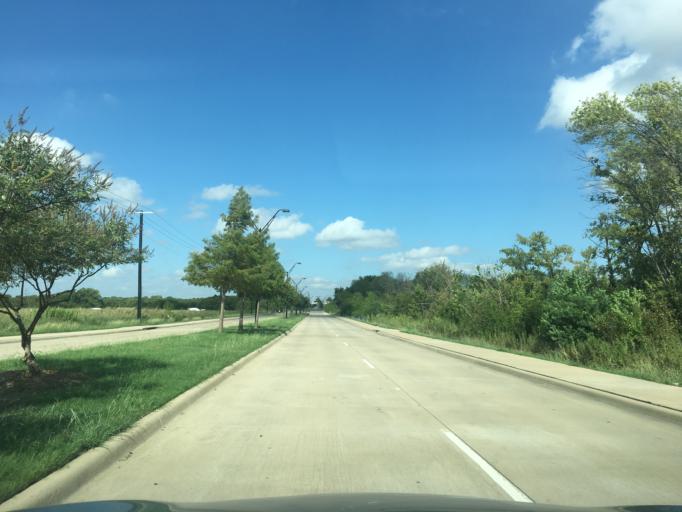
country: US
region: Texas
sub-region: Dallas County
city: Sachse
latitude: 32.9560
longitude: -96.5916
